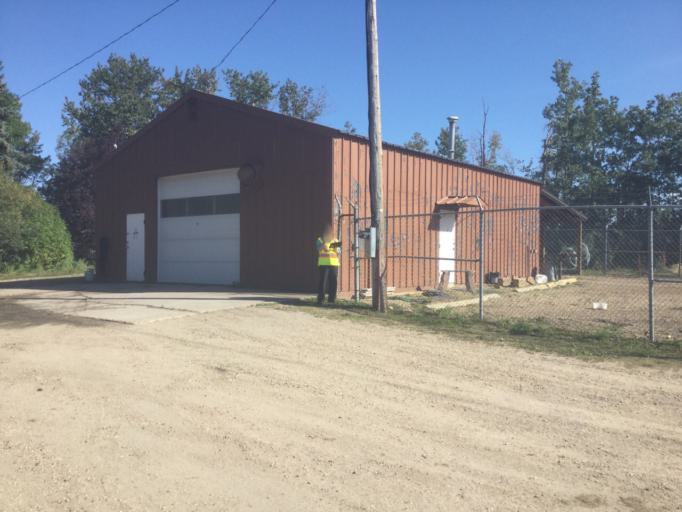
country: CA
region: Alberta
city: Sylvan Lake
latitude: 52.4537
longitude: -113.9708
